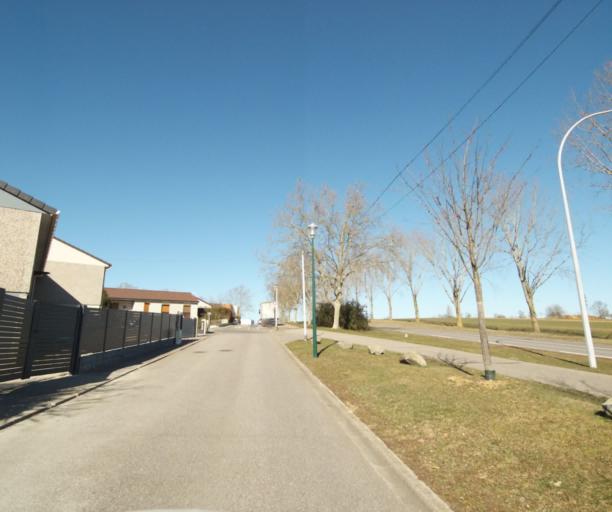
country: FR
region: Lorraine
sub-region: Departement de Meurthe-et-Moselle
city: Heillecourt
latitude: 48.6449
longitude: 6.2097
